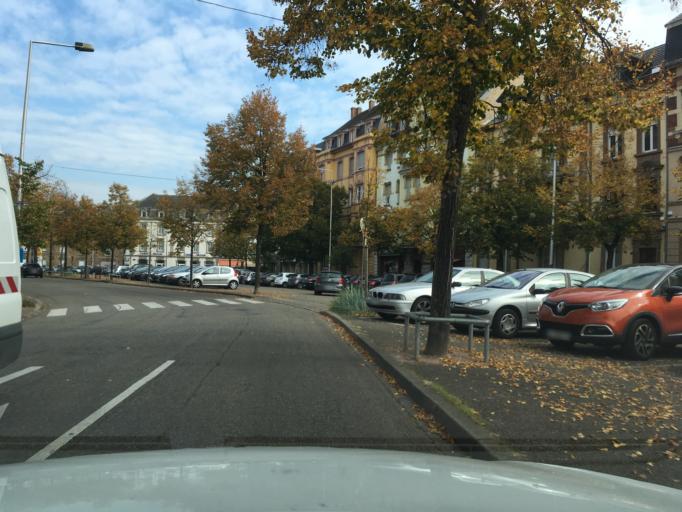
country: FR
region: Alsace
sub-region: Departement du Haut-Rhin
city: Colmar
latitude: 48.0813
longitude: 7.3470
